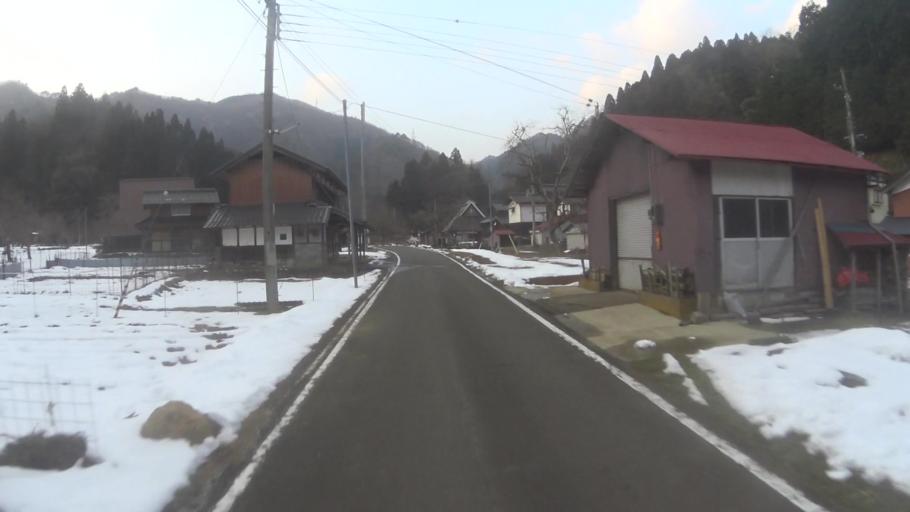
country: JP
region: Kyoto
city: Maizuru
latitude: 35.4359
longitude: 135.4731
